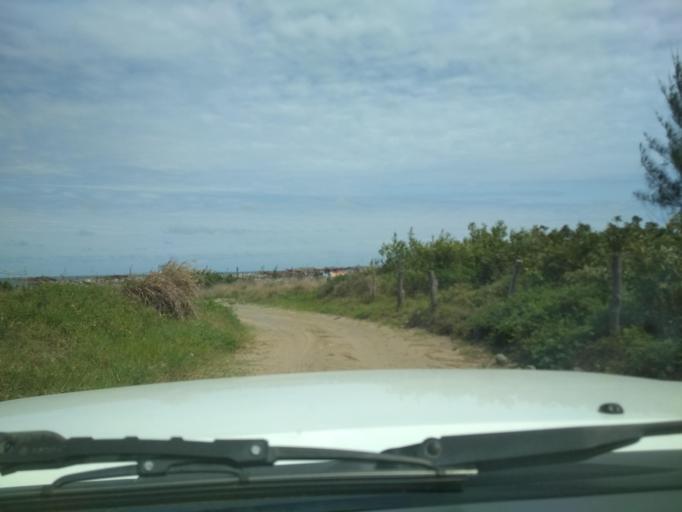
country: MX
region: Veracruz
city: Anton Lizardo
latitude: 19.0229
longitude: -95.9677
